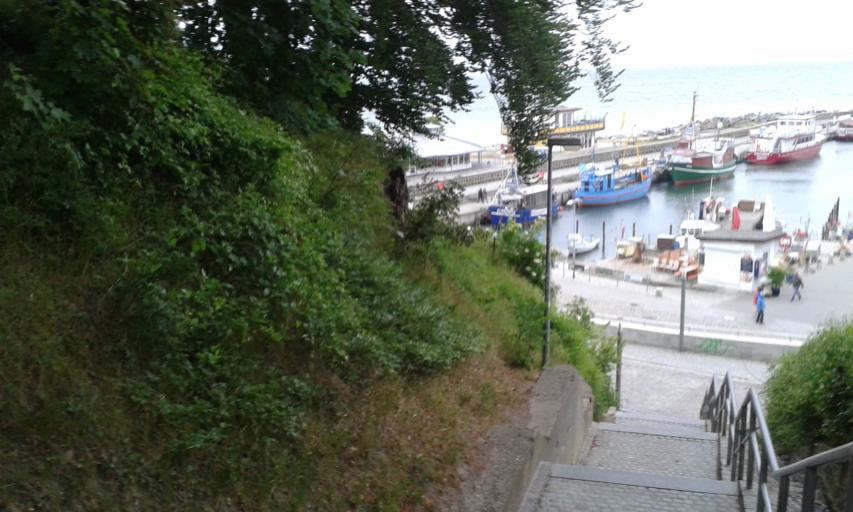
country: DE
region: Mecklenburg-Vorpommern
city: Sassnitz
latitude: 54.5156
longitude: 13.6498
